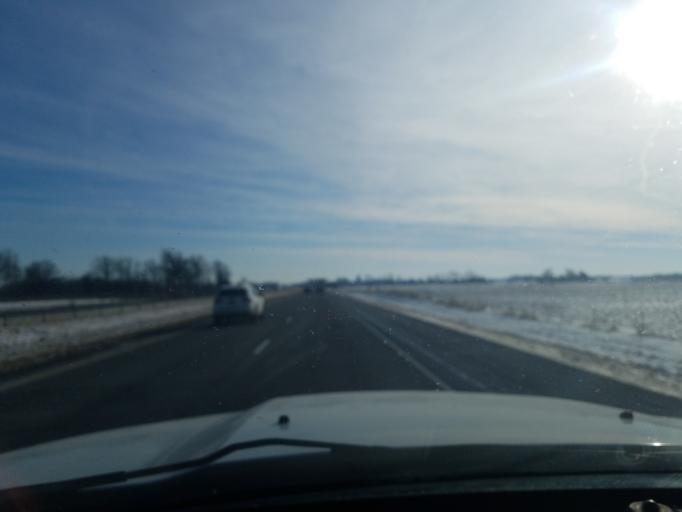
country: US
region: Indiana
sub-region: Grant County
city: Fairmount
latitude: 40.3424
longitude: -85.5591
